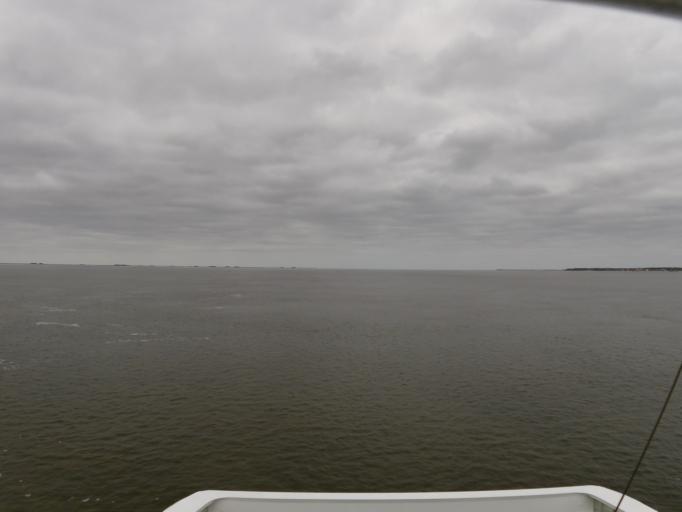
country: DE
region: Schleswig-Holstein
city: Wyk auf Fohr
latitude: 54.6937
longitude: 8.6281
